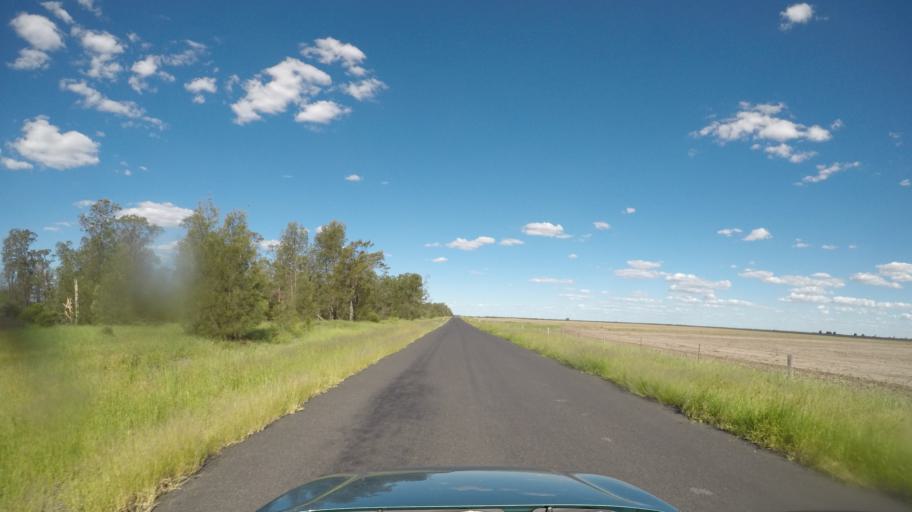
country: AU
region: Queensland
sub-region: Goondiwindi
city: Goondiwindi
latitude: -28.1530
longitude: 150.3511
